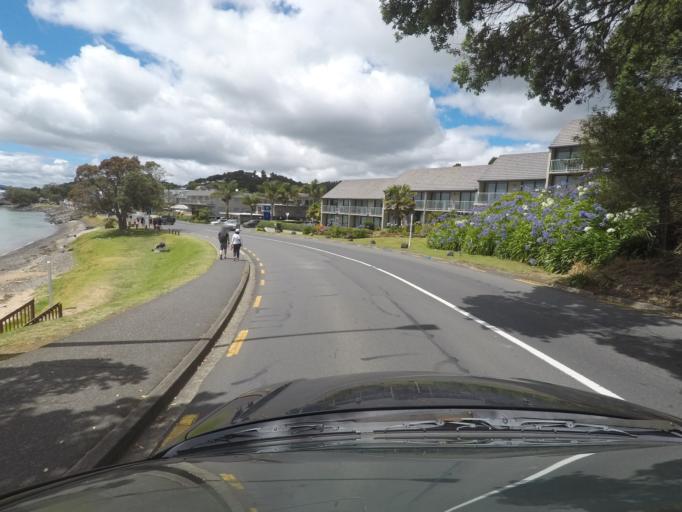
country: NZ
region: Northland
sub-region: Far North District
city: Paihia
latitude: -35.2794
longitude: 174.0896
